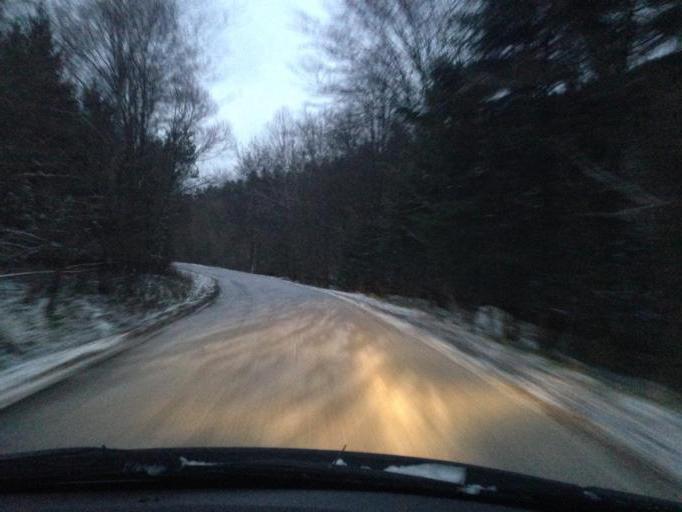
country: PL
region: Subcarpathian Voivodeship
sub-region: Powiat jasielski
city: Krempna
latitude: 49.5127
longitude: 21.5419
